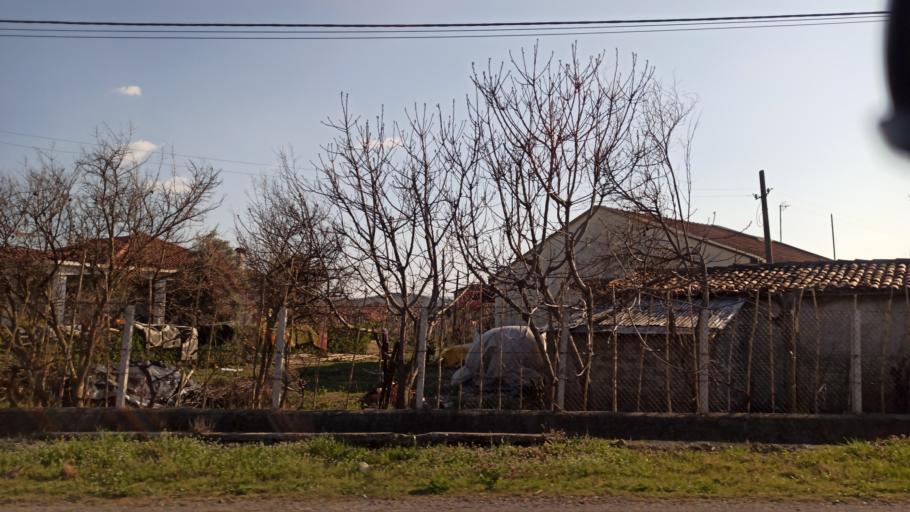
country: AL
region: Shkoder
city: Vukatane
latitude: 41.9905
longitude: 19.5764
